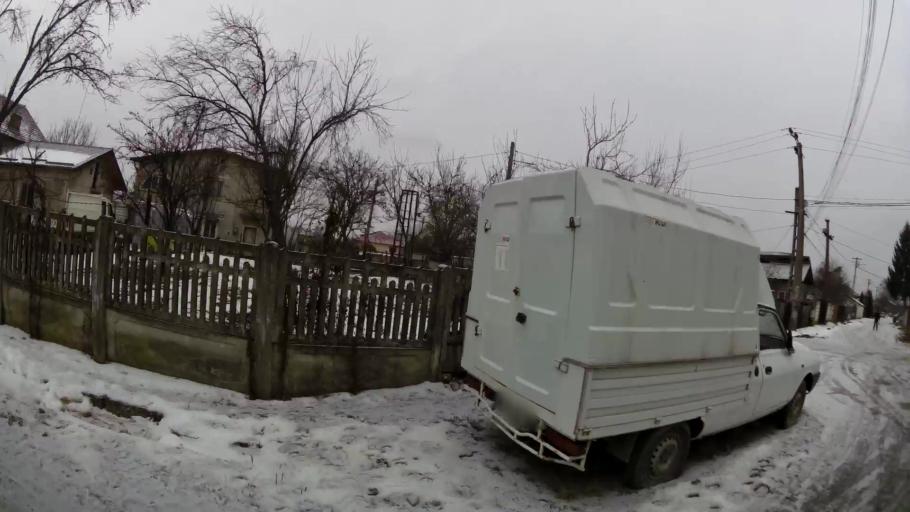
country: RO
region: Dambovita
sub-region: Municipiul Targoviste
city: Targoviste
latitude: 44.9361
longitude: 25.4737
